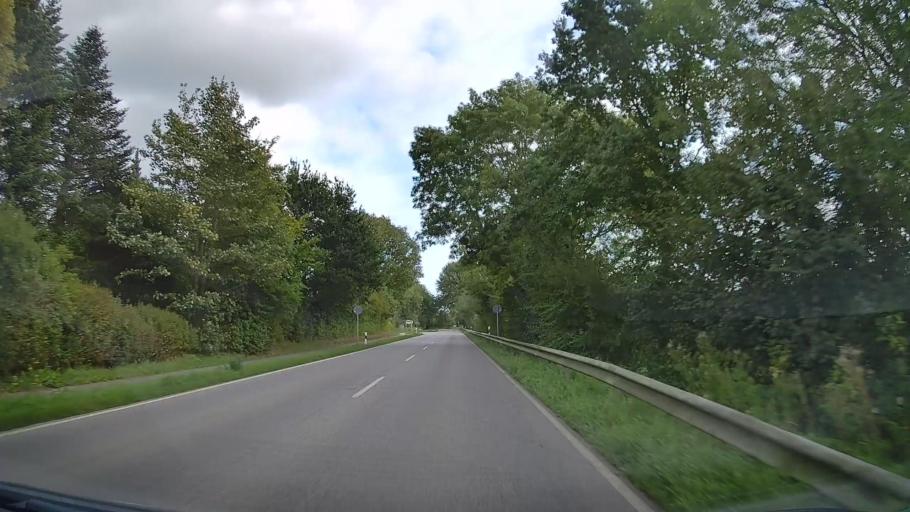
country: DE
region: Schleswig-Holstein
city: Niesgrau
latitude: 54.7503
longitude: 9.8293
